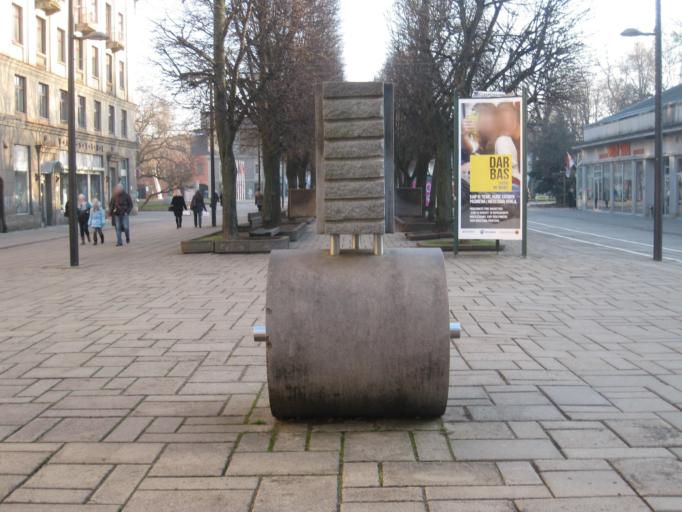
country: LT
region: Kauno apskritis
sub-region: Kaunas
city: Kaunas
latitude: 54.8978
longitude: 23.9036
